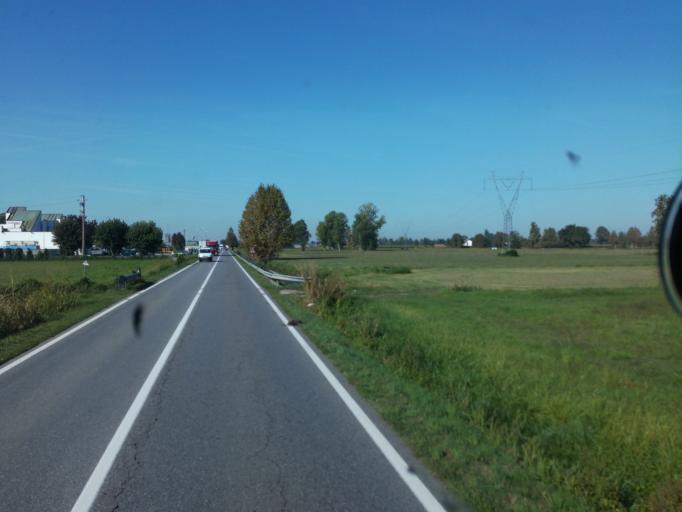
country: IT
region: Lombardy
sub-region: Provincia di Cremona
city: Chieve
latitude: 45.3494
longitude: 9.6065
